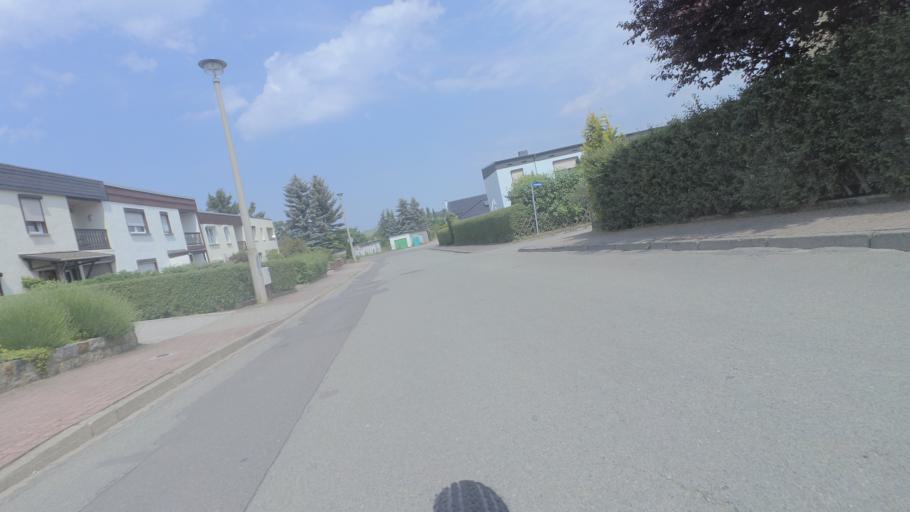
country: DE
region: Saxony-Anhalt
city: Thale
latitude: 51.7468
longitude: 11.0575
